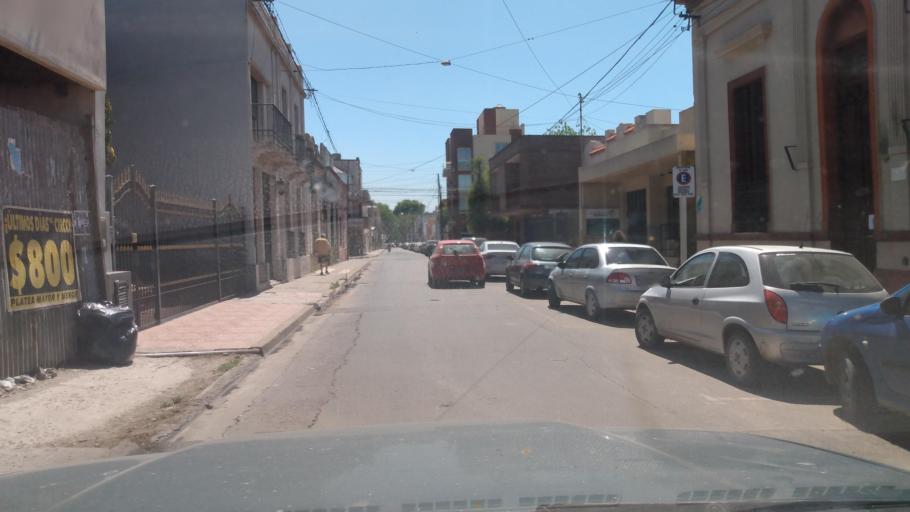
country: AR
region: Buenos Aires
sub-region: Partido de Lujan
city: Lujan
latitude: -34.5640
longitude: -59.1145
